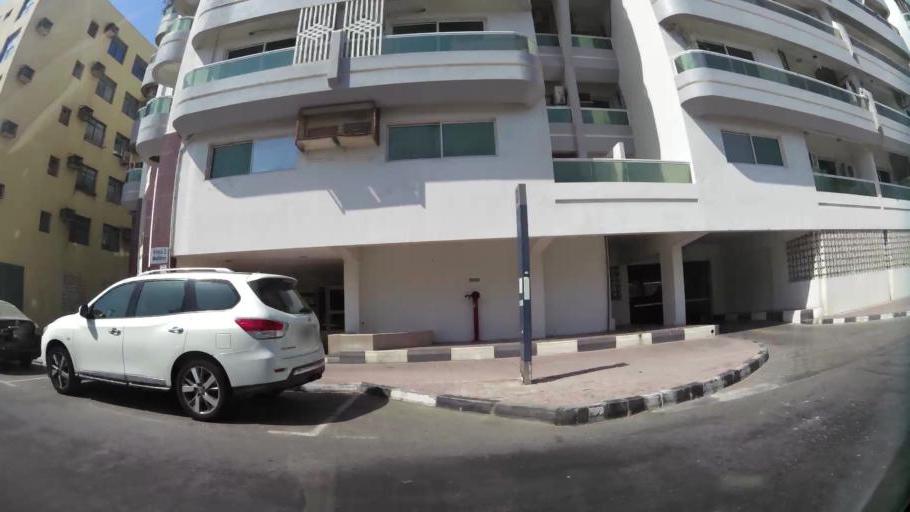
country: AE
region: Ash Shariqah
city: Sharjah
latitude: 25.2679
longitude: 55.3754
